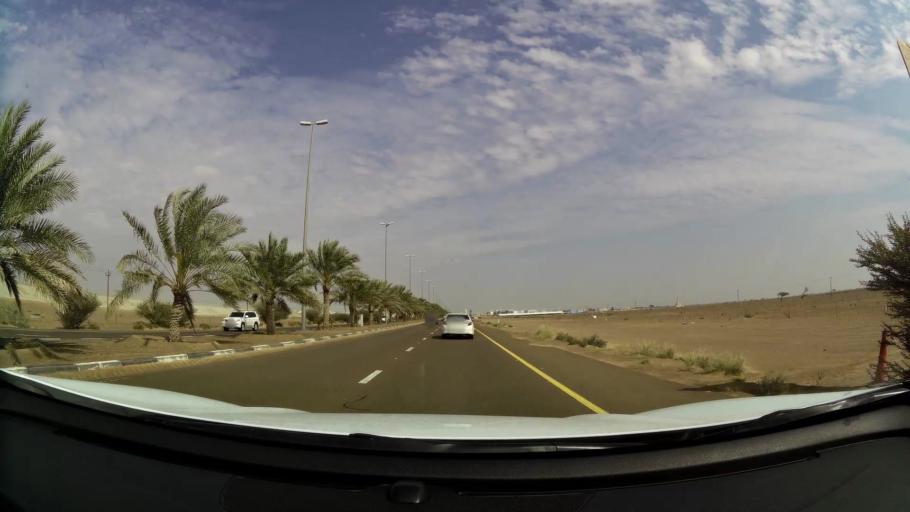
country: AE
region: Abu Dhabi
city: Al Ain
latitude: 24.0927
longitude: 55.8817
